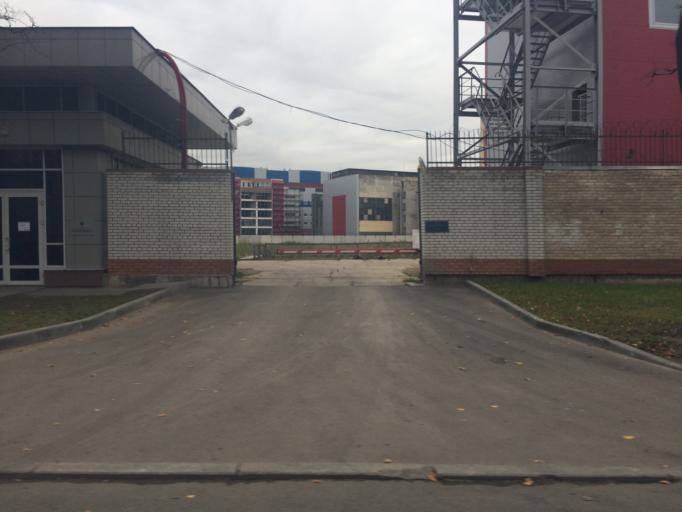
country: RU
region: Leningrad
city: Rybatskoye
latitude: 59.8591
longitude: 30.4793
